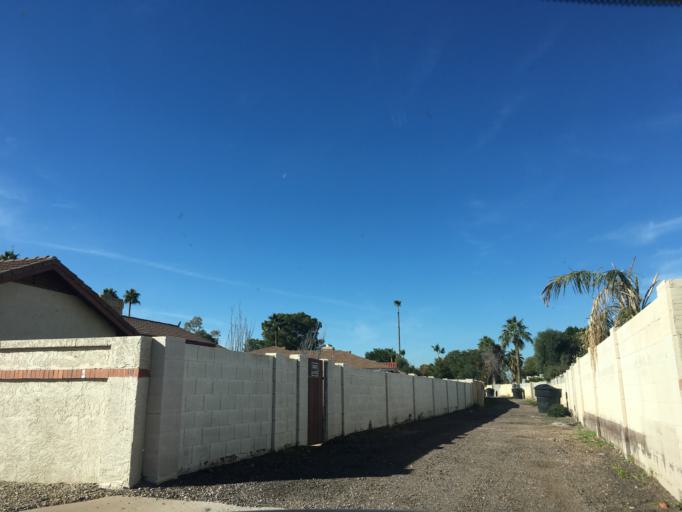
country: US
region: Arizona
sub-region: Maricopa County
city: Tempe
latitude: 33.3893
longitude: -111.9049
